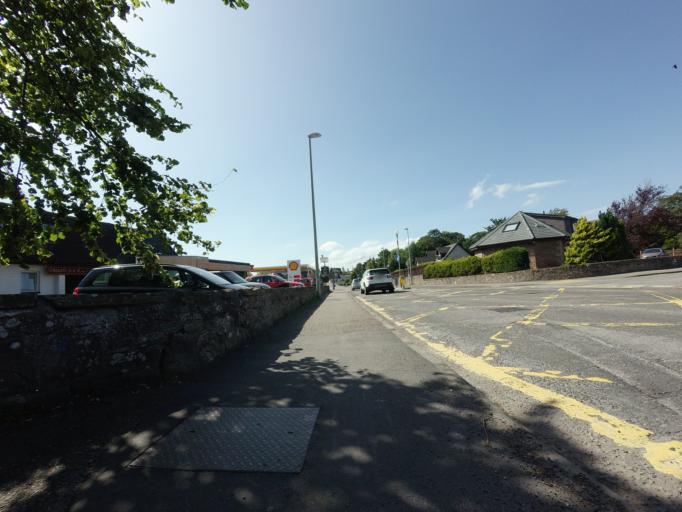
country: GB
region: Scotland
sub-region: Highland
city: Inverness
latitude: 57.4729
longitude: -4.1970
